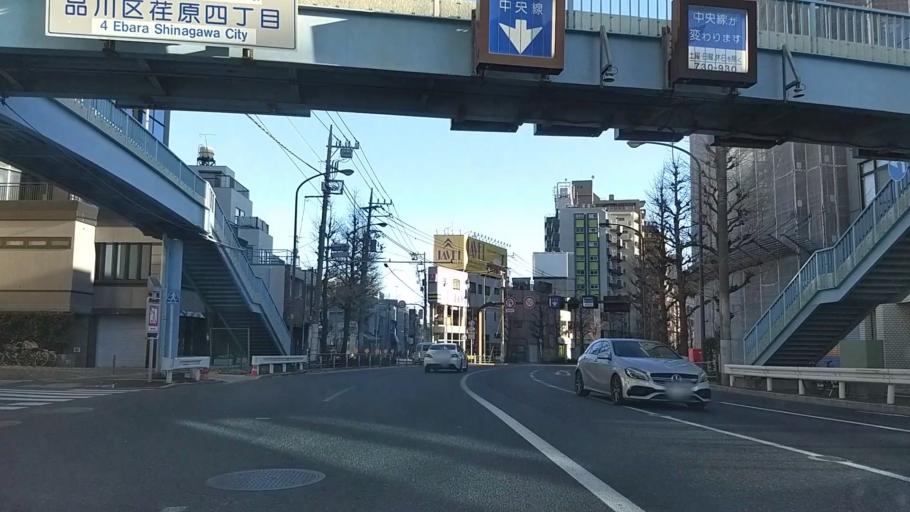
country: JP
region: Tokyo
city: Tokyo
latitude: 35.6157
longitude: 139.7089
